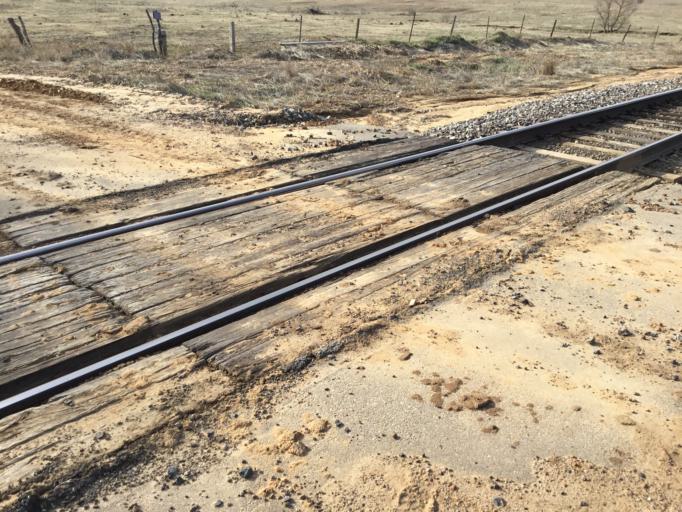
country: US
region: Kansas
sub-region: Ellsworth County
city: Ellsworth
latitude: 38.7405
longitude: -98.0128
